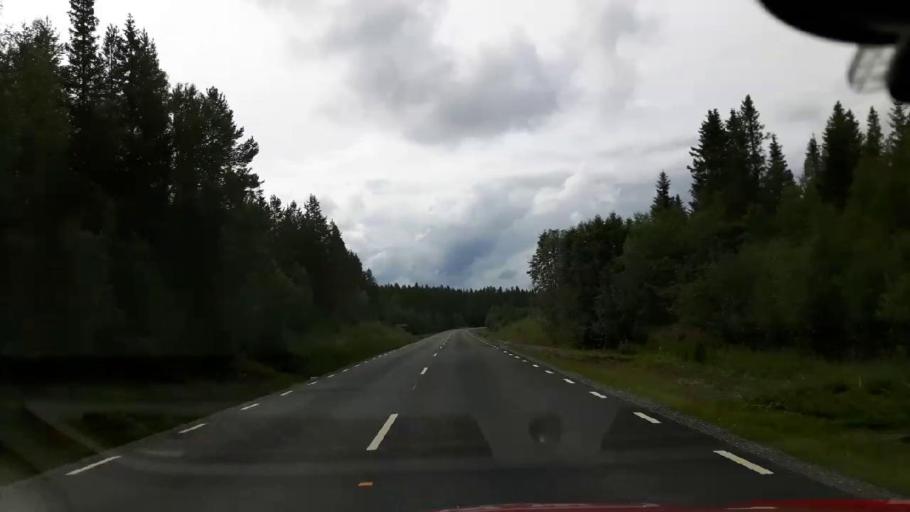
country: NO
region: Nord-Trondelag
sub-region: Lierne
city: Sandvika
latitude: 64.6318
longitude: 14.1383
